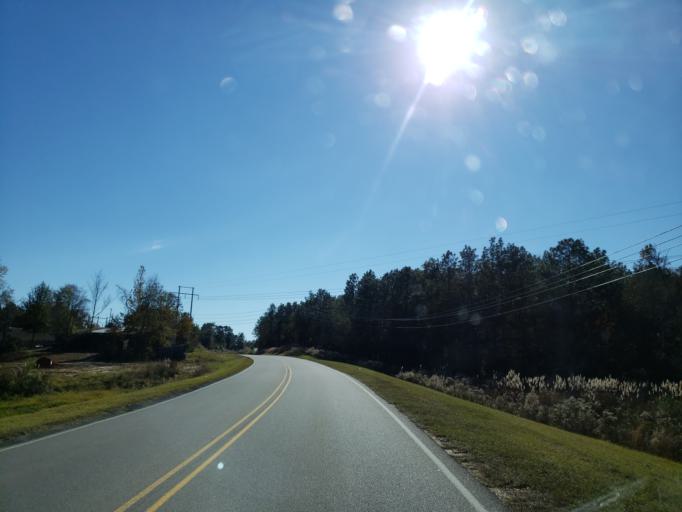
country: US
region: Mississippi
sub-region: Lamar County
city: Arnold Line
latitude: 31.3351
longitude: -89.3987
